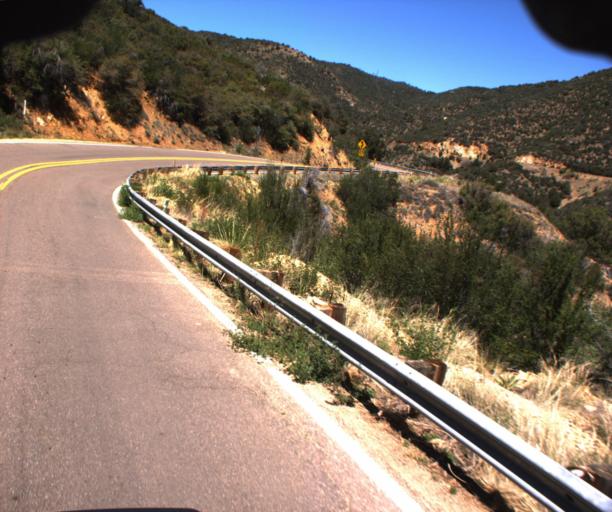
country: US
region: Arizona
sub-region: Yavapai County
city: Prescott
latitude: 34.4620
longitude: -112.5171
